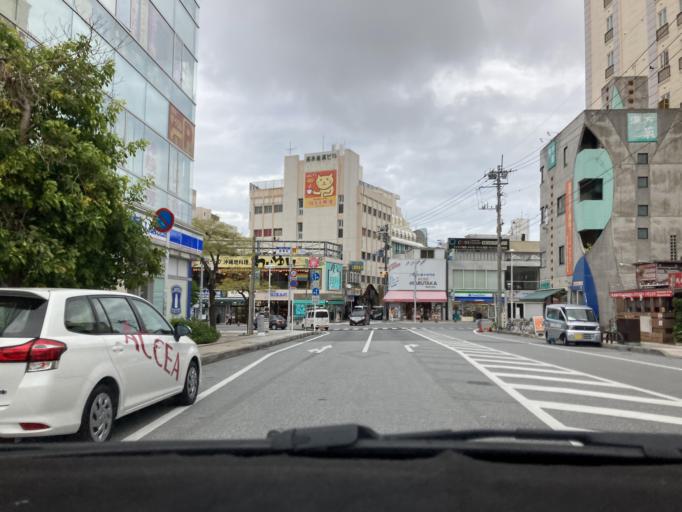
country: JP
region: Okinawa
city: Naha-shi
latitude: 26.2162
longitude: 127.6896
